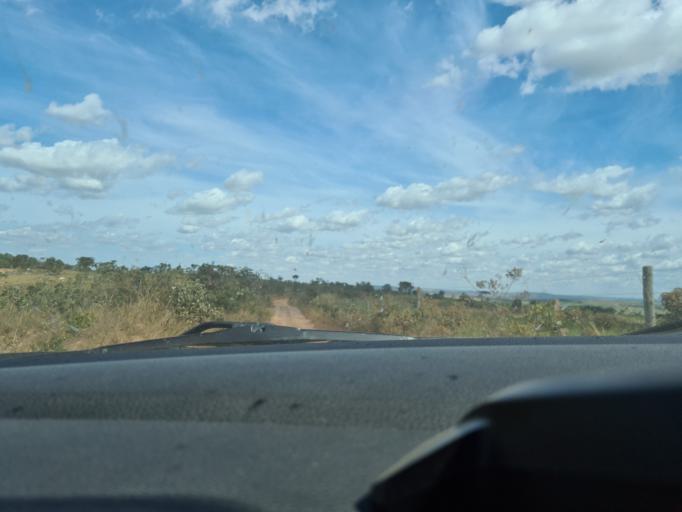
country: BR
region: Goias
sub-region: Silvania
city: Silvania
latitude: -16.5403
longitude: -48.5674
